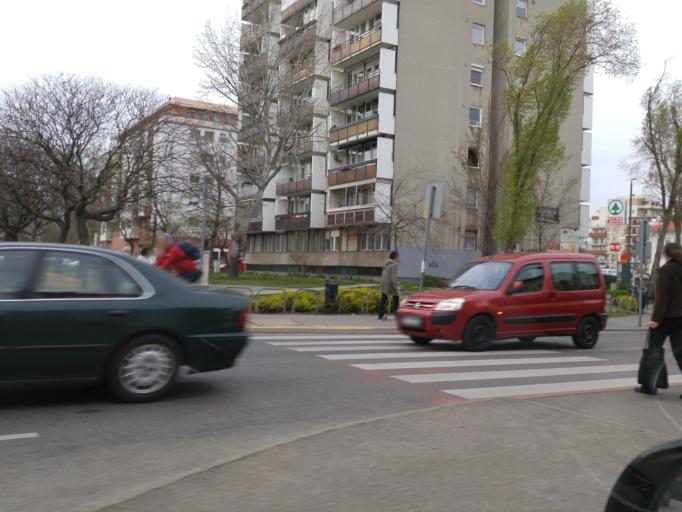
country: HU
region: Budapest
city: Budapest XX. keruelet
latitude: 47.4374
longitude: 19.1007
